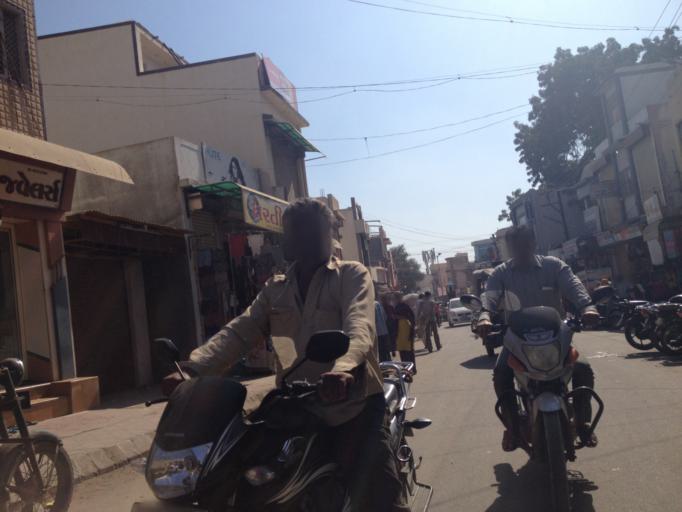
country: IN
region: Gujarat
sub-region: Kachchh
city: Anjar
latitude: 23.1139
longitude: 70.0279
